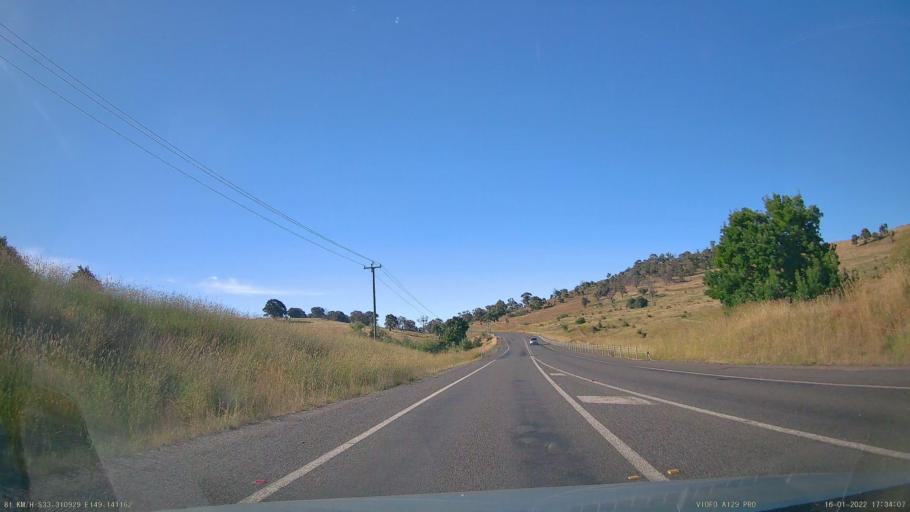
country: AU
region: New South Wales
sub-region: Orange Municipality
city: Orange
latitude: -33.3107
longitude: 149.1412
